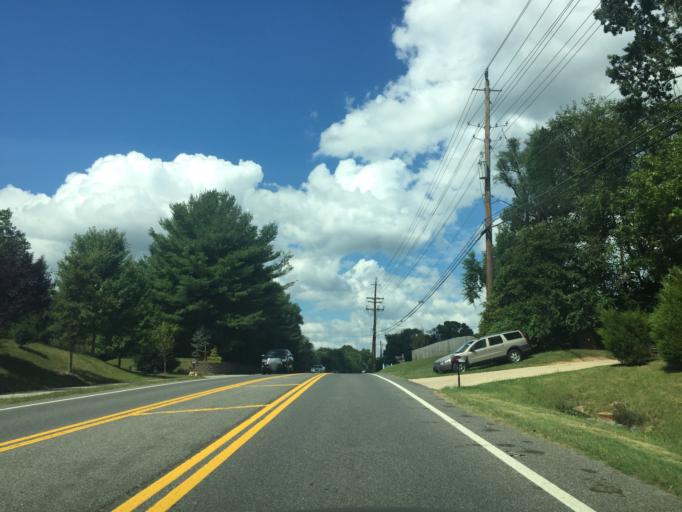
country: US
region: Maryland
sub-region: Montgomery County
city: Rossmoor
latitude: 39.1194
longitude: -77.1076
